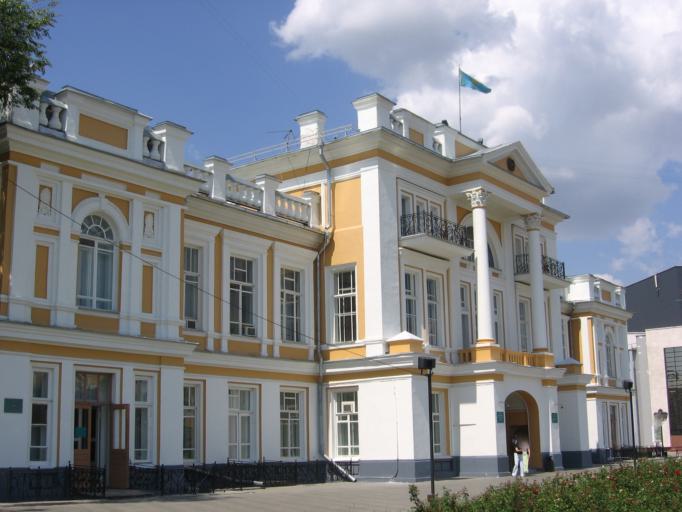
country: KZ
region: Batys Qazaqstan
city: Oral
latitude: 51.2035
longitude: 51.3701
